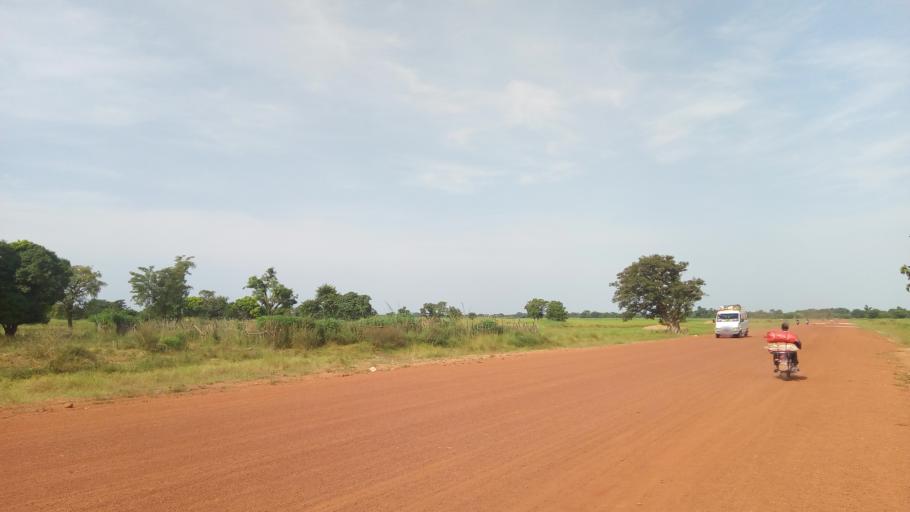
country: ML
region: Koulikoro
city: Kangaba
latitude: 11.6796
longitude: -8.7100
